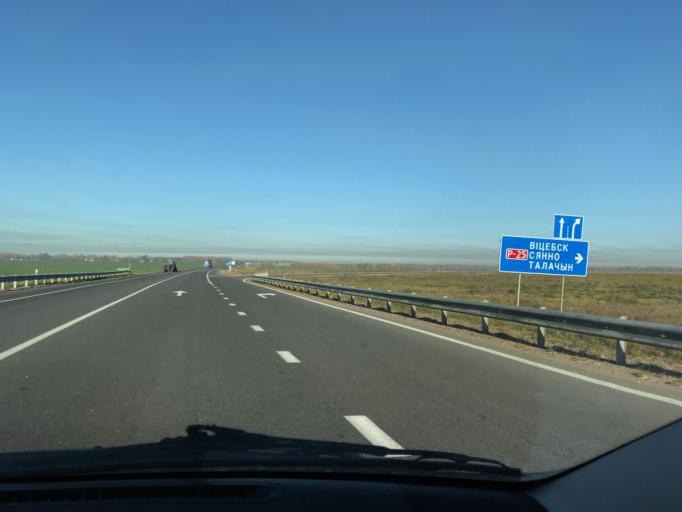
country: BY
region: Vitebsk
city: Vitebsk
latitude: 55.1103
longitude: 30.1043
